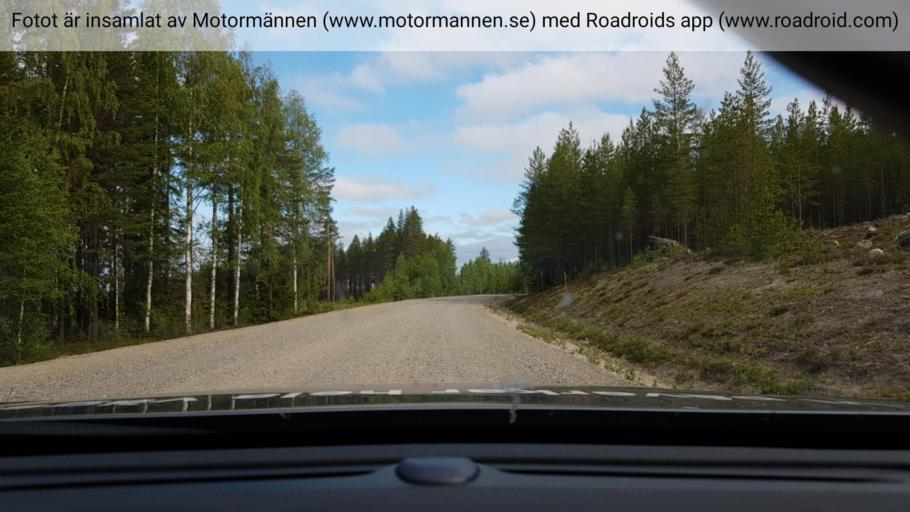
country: SE
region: Vaesterbotten
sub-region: Norsjo Kommun
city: Norsjoe
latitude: 64.6226
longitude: 19.2859
